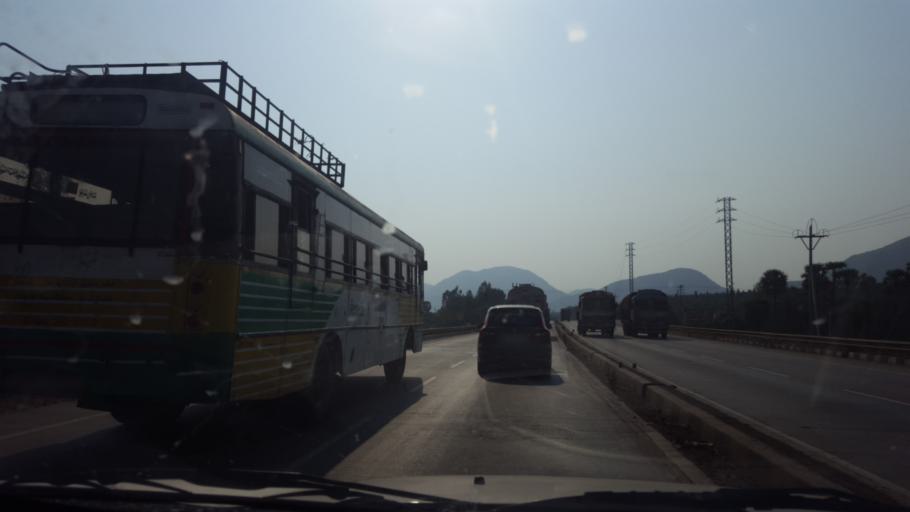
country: IN
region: Andhra Pradesh
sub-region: Vishakhapatnam
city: Anakapalle
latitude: 17.6479
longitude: 82.9137
